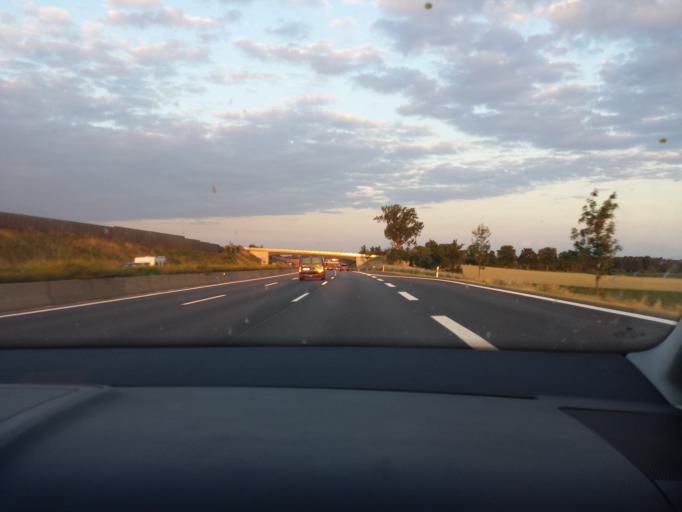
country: DE
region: Bavaria
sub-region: Upper Bavaria
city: Maisach
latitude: 48.2554
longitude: 11.3044
